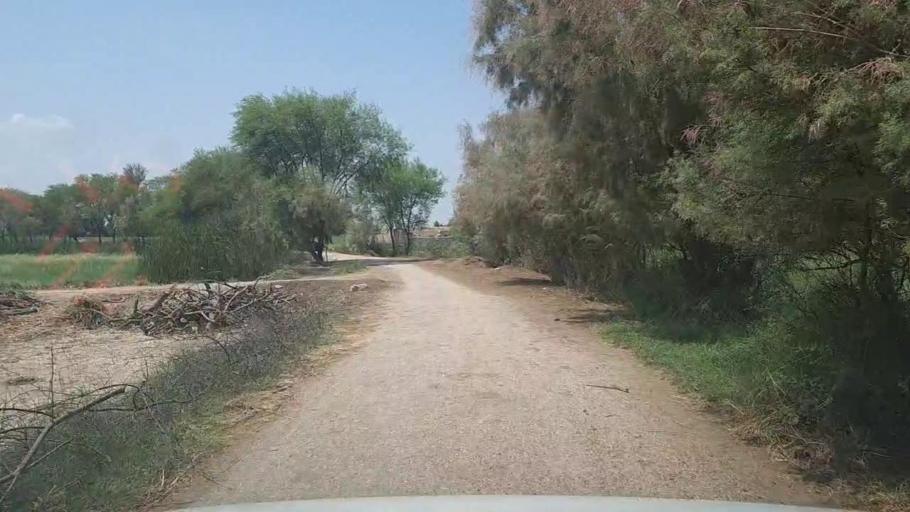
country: PK
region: Sindh
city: Ubauro
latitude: 28.1786
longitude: 69.7088
